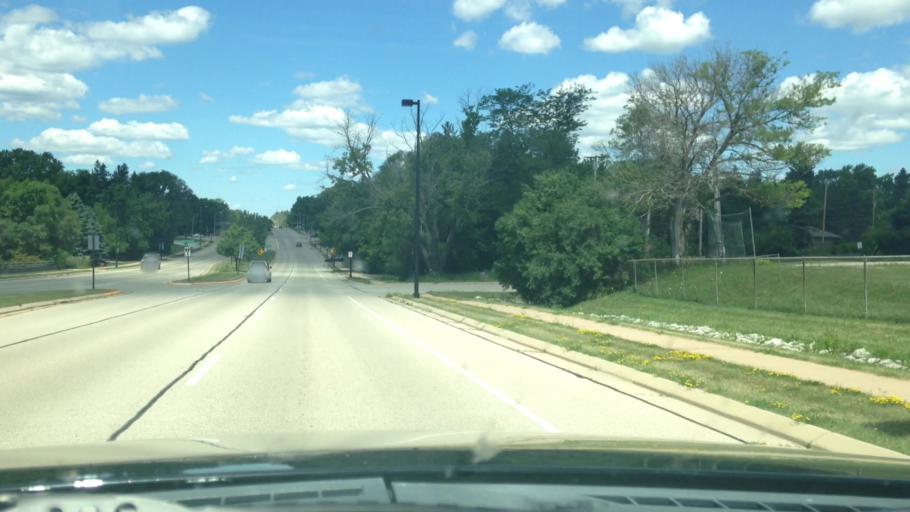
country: US
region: Wisconsin
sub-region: Waukesha County
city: Menomonee Falls
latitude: 43.1530
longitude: -88.0807
